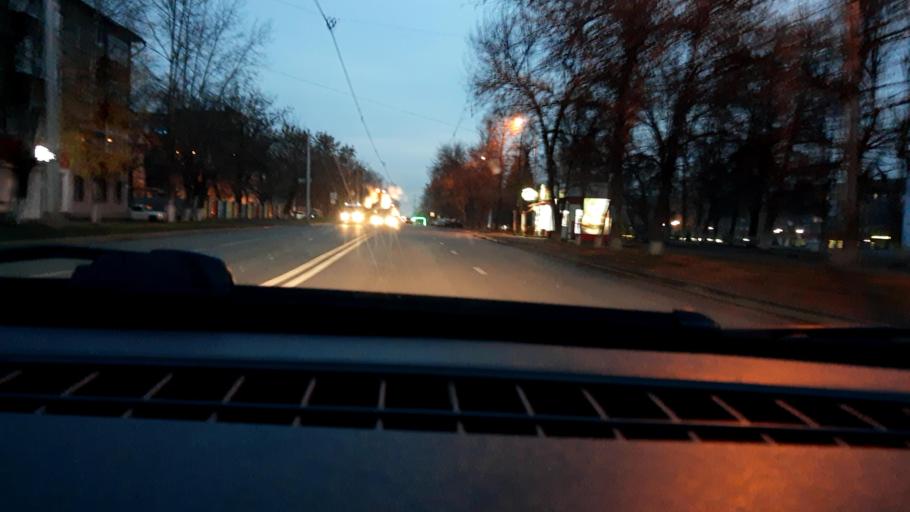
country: RU
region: Bashkortostan
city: Ufa
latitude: 54.8191
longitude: 56.1077
